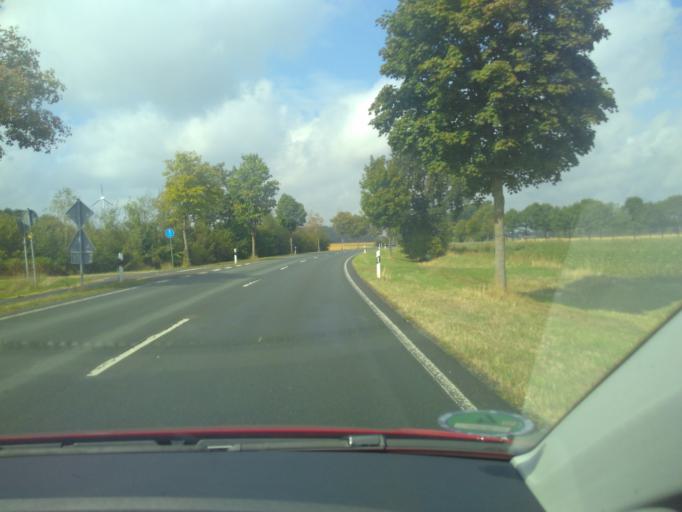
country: DE
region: North Rhine-Westphalia
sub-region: Regierungsbezirk Munster
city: Ostbevern
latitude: 52.0166
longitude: 7.9059
